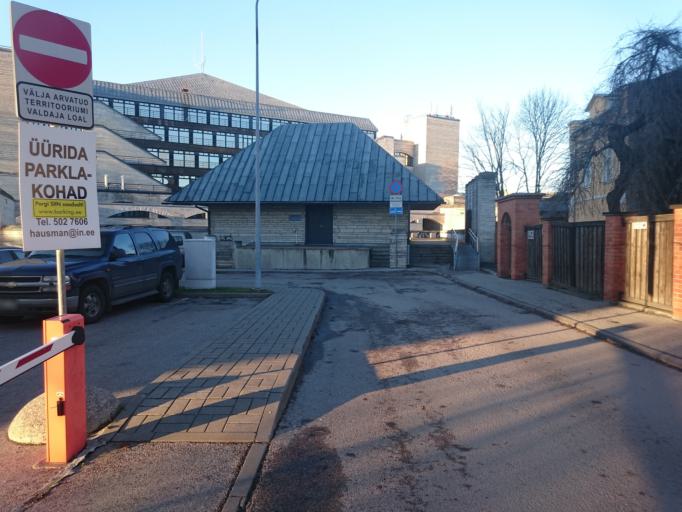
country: EE
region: Harju
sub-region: Tallinna linn
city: Tallinn
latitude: 59.4297
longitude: 24.7403
